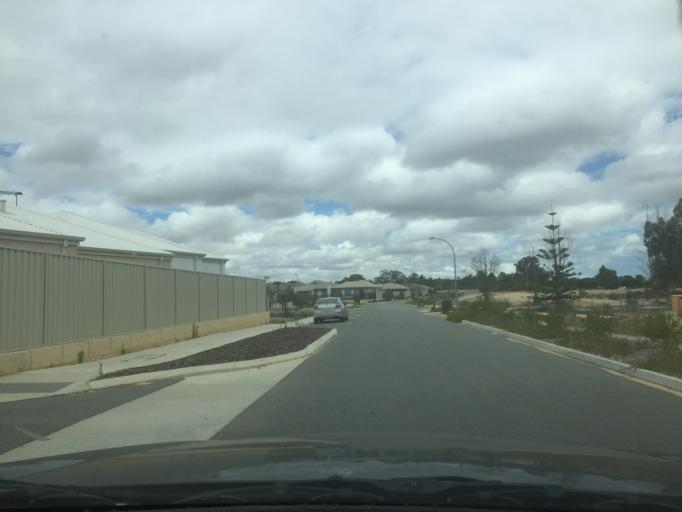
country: AU
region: Western Australia
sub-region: Armadale
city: Harrisdale
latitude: -32.1369
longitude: 115.9063
